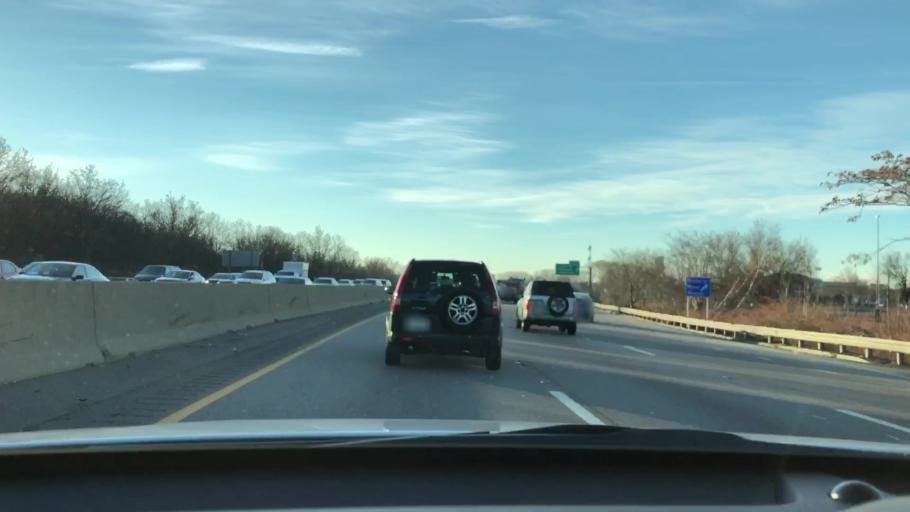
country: US
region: Massachusetts
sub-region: Norfolk County
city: Braintree
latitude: 42.2155
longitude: -70.9971
